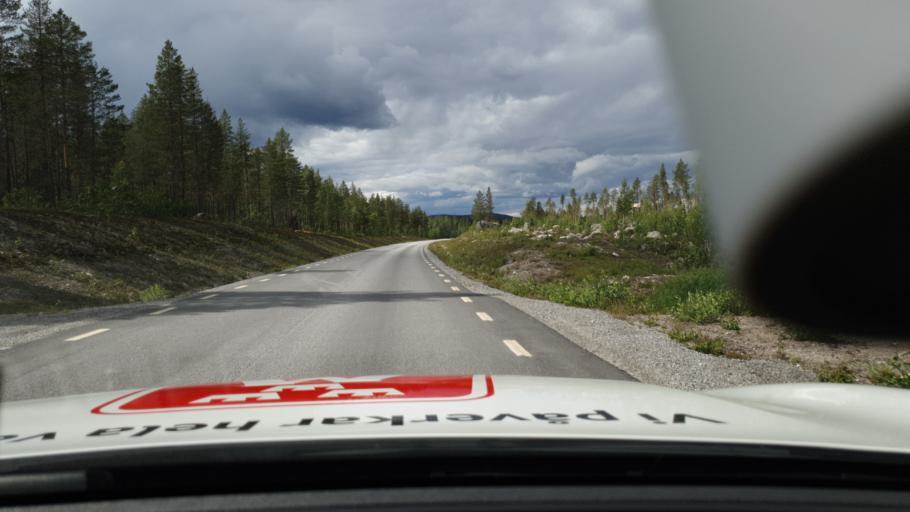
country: SE
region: Norrbotten
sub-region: Jokkmokks Kommun
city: Jokkmokk
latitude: 66.8194
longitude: 19.1604
